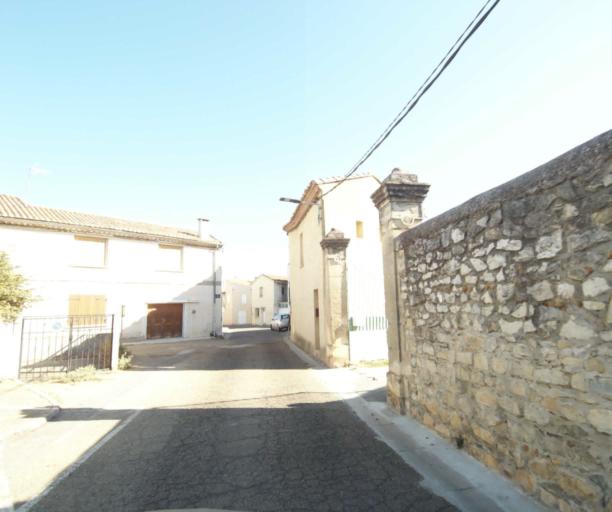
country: FR
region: Languedoc-Roussillon
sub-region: Departement du Gard
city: Bouillargues
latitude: 43.7986
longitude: 4.4270
